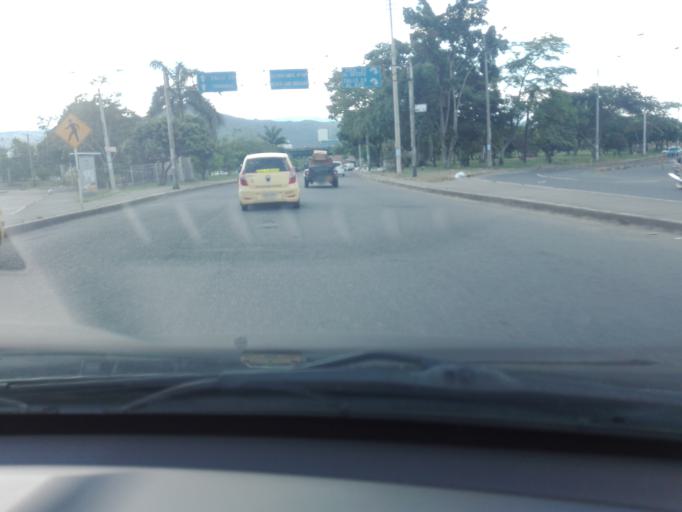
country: CO
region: Valle del Cauca
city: Cali
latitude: 3.4433
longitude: -76.5173
